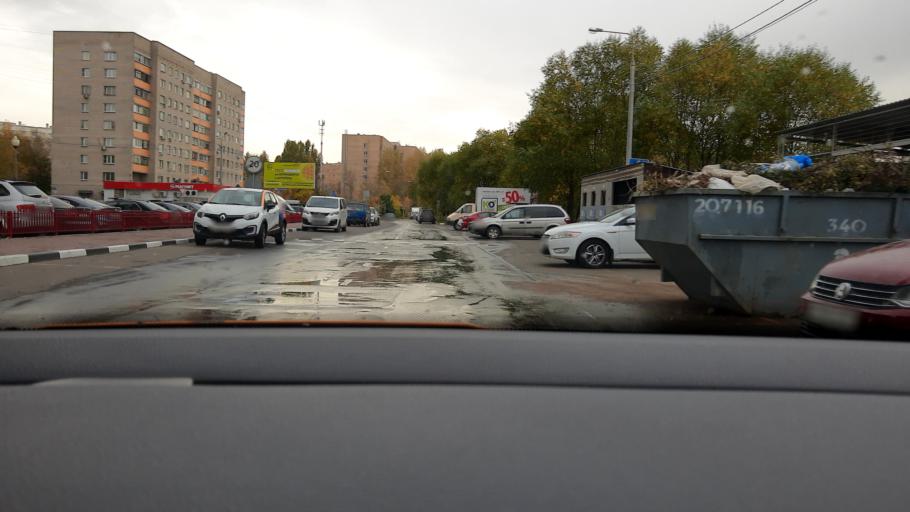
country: RU
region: Moscow
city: Ivanovskoye
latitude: 55.7716
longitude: 37.8461
